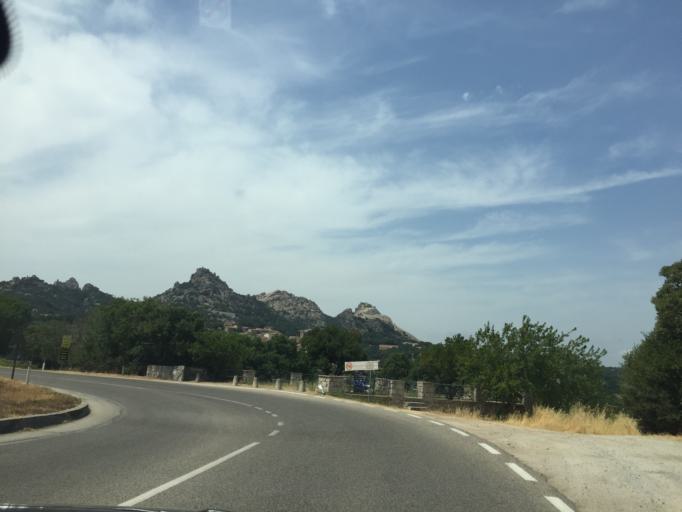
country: IT
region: Sardinia
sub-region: Provincia di Olbia-Tempio
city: Aggius
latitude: 40.9230
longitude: 9.0699
